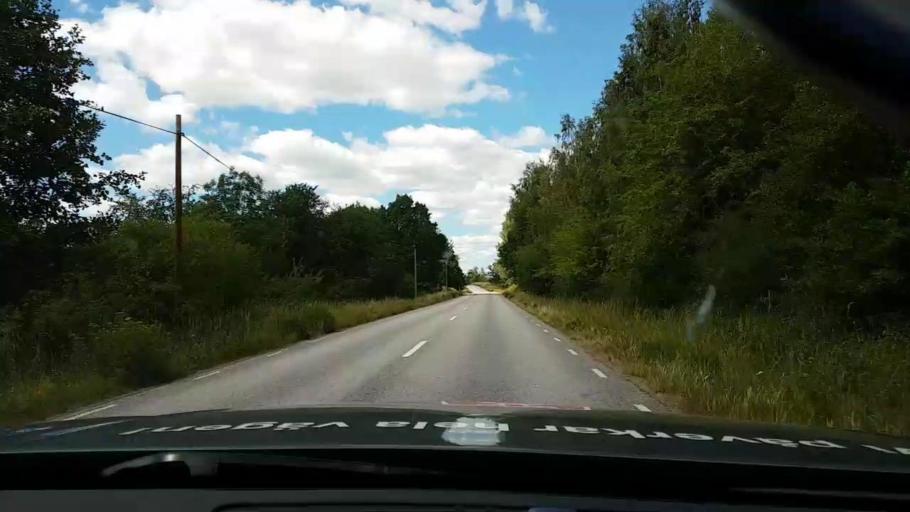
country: SE
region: Kalmar
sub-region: Vasterviks Kommun
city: Forserum
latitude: 58.0397
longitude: 16.4334
